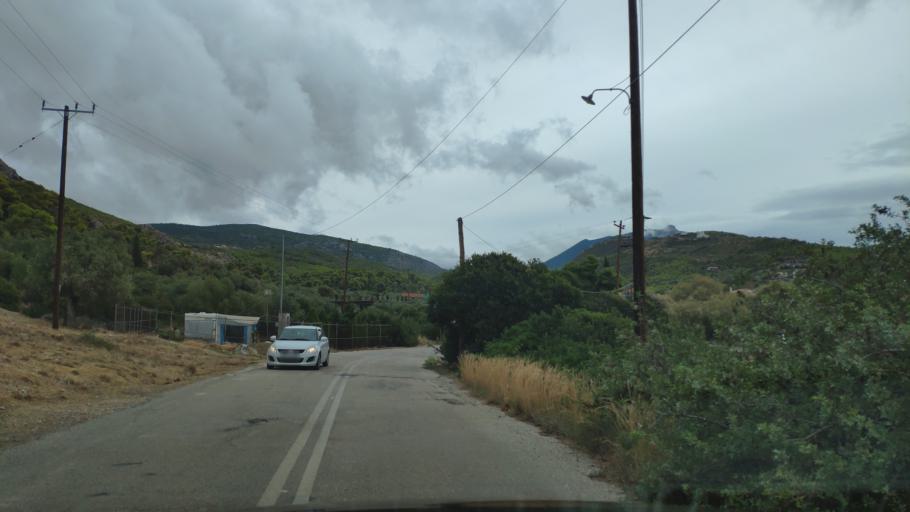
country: GR
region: Peloponnese
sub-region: Nomos Korinthias
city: Perachora
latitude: 38.0330
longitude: 22.8926
